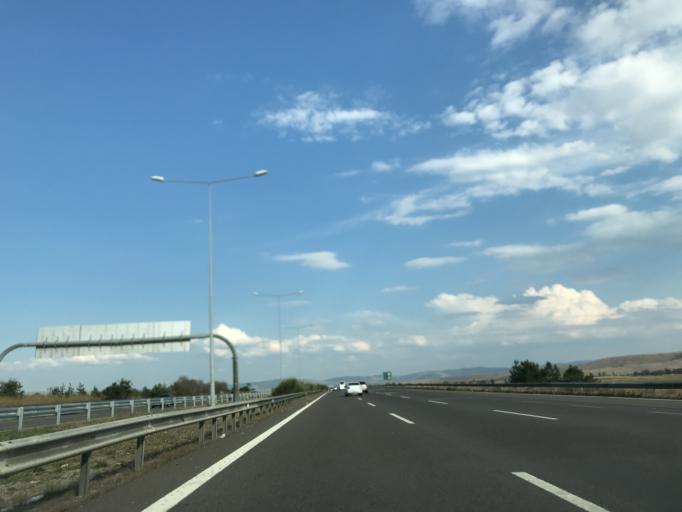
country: TR
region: Bolu
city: Dortdivan
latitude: 40.7416
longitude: 32.1266
